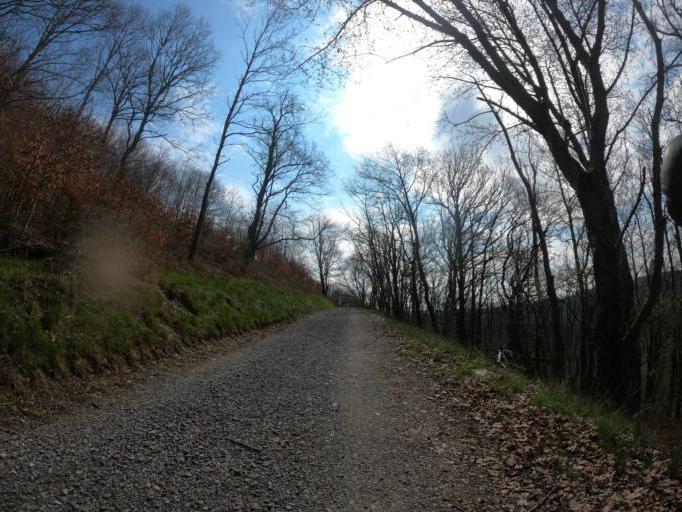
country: DE
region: North Rhine-Westphalia
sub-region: Regierungsbezirk Koln
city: Simmerath
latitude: 50.5863
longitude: 6.3689
